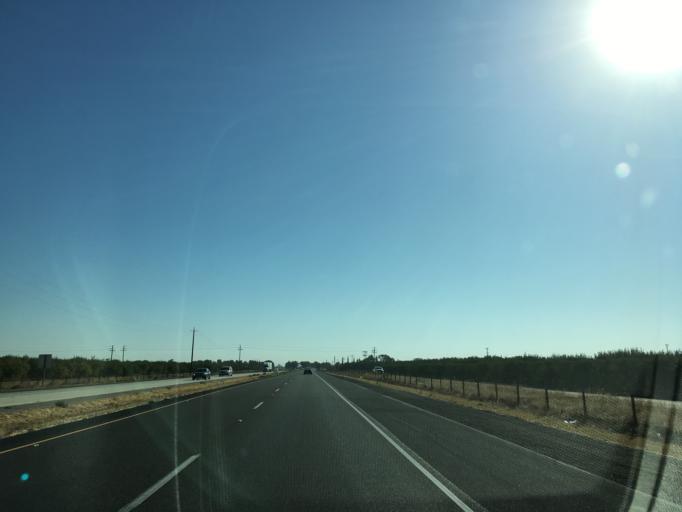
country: US
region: California
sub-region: Madera County
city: Fairmead
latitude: 37.0838
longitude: -120.2238
